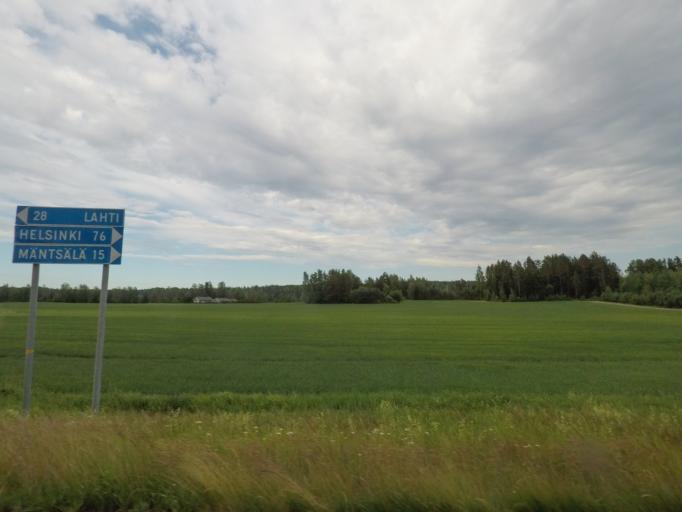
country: FI
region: Uusimaa
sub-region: Helsinki
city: Maentsaelae
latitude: 60.7522
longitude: 25.4322
